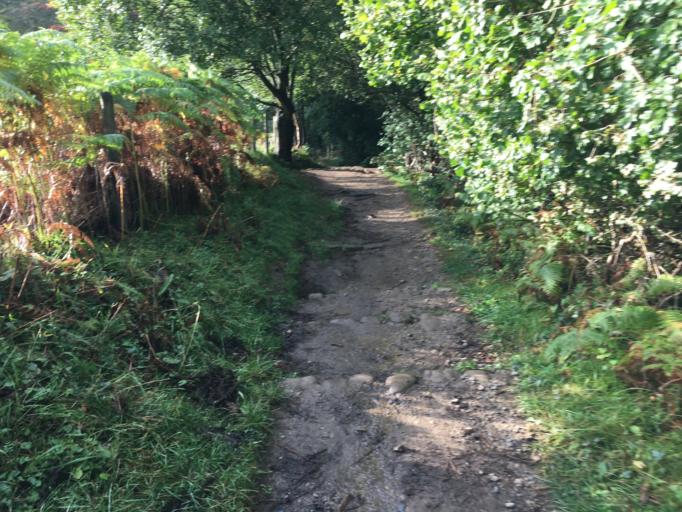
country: GB
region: England
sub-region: North Yorkshire
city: Sleights
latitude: 54.3984
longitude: -0.7296
